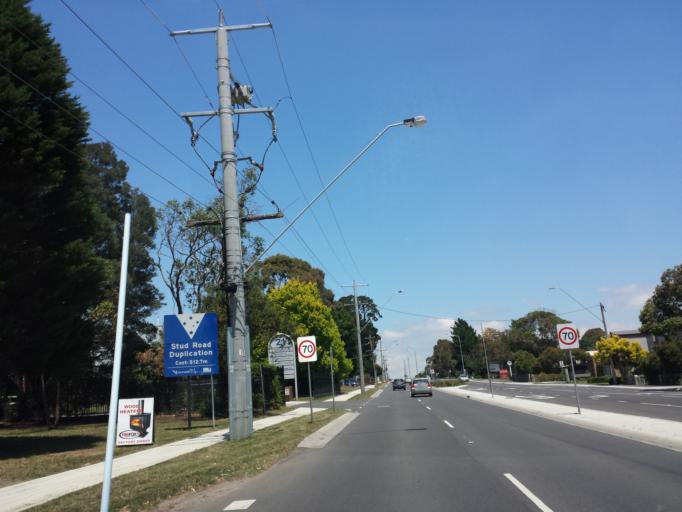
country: AU
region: Victoria
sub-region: Maroondah
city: Heathmont
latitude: -37.8444
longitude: 145.2481
